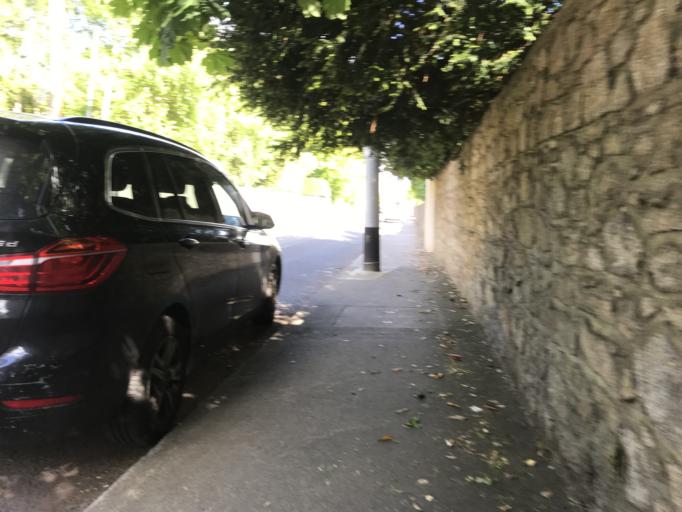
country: IE
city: Booterstown
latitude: 53.2985
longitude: -6.1994
